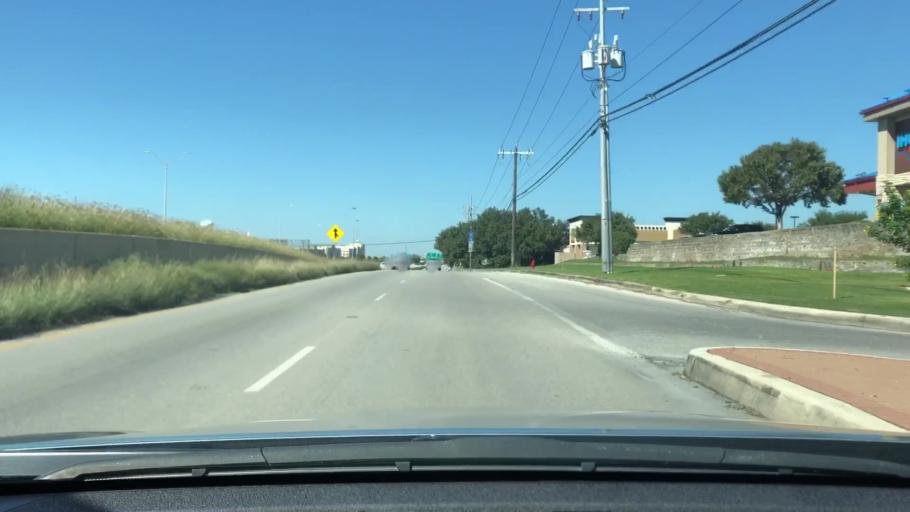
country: US
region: Texas
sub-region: Bexar County
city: Live Oak
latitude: 29.5625
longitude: -98.3281
